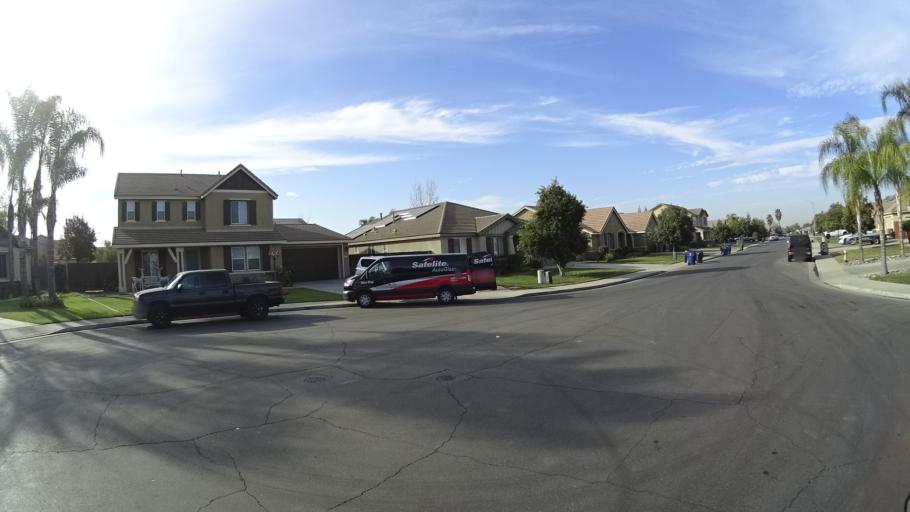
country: US
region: California
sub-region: Kern County
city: Rosedale
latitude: 35.4067
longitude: -119.1373
